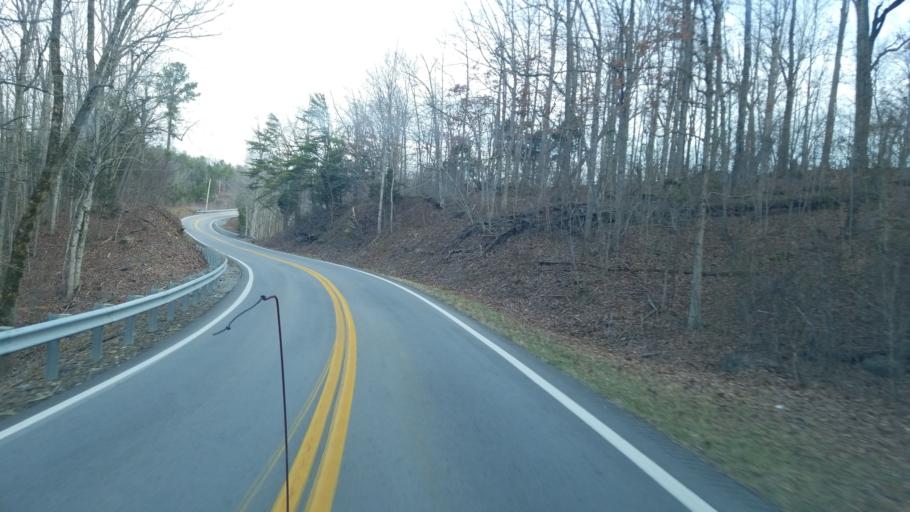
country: US
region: Kentucky
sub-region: Clinton County
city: Albany
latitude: 36.8482
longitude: -85.1610
